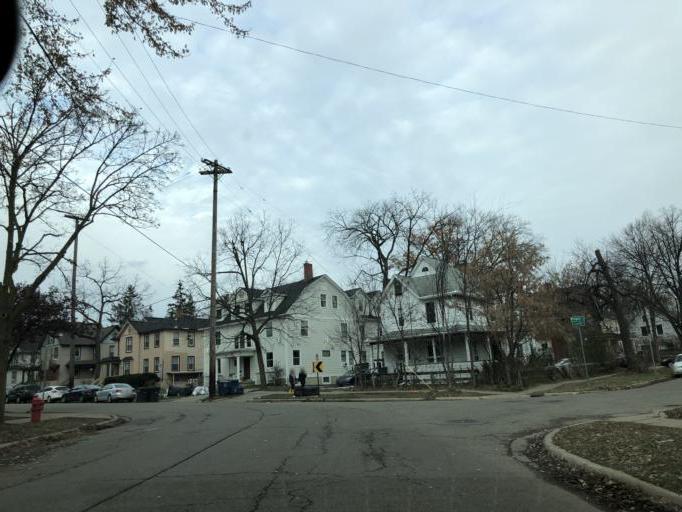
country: US
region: Michigan
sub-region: Washtenaw County
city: Ann Arbor
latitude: 42.2685
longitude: -83.7359
